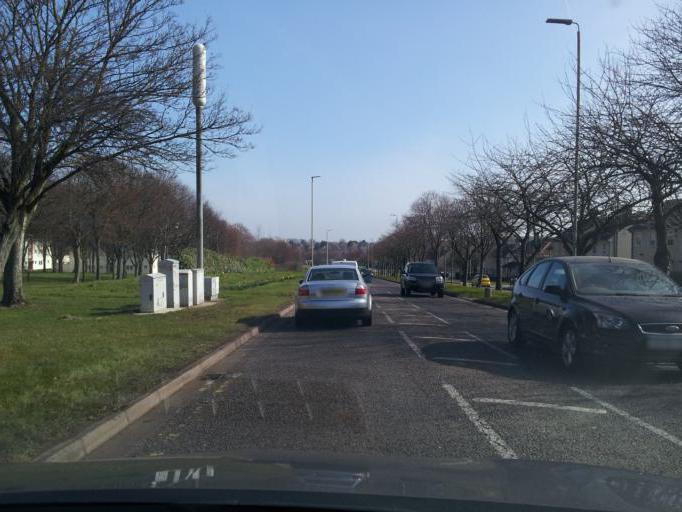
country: GB
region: England
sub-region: Leicestershire
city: Blaby
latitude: 52.5955
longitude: -1.1534
